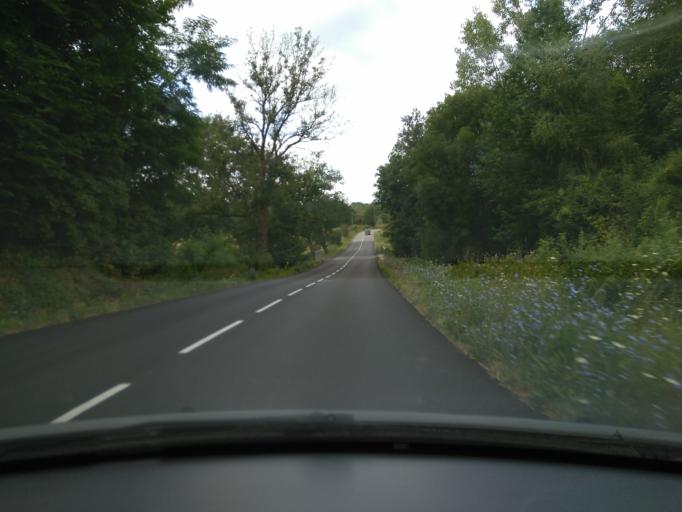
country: FR
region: Rhone-Alpes
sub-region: Departement de l'Isere
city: Beaurepaire
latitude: 45.3989
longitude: 5.1352
